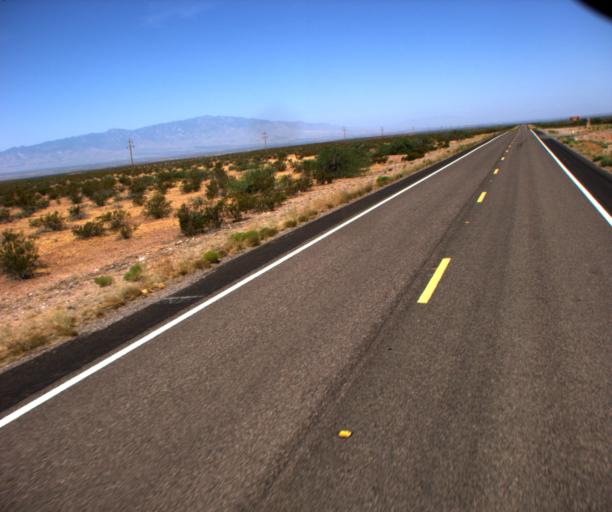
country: US
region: Arizona
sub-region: Graham County
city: Swift Trail Junction
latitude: 32.7601
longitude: -109.4380
